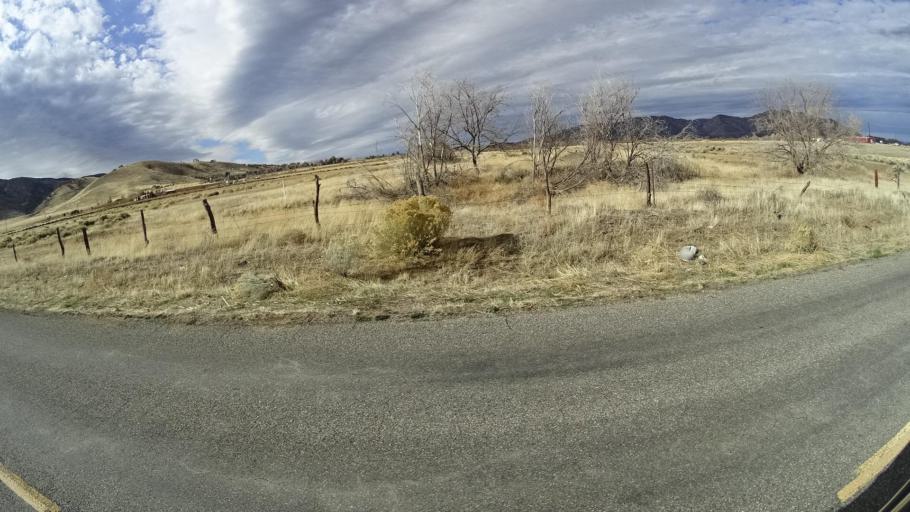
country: US
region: California
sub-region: Kern County
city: Tehachapi
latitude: 35.1131
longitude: -118.4678
